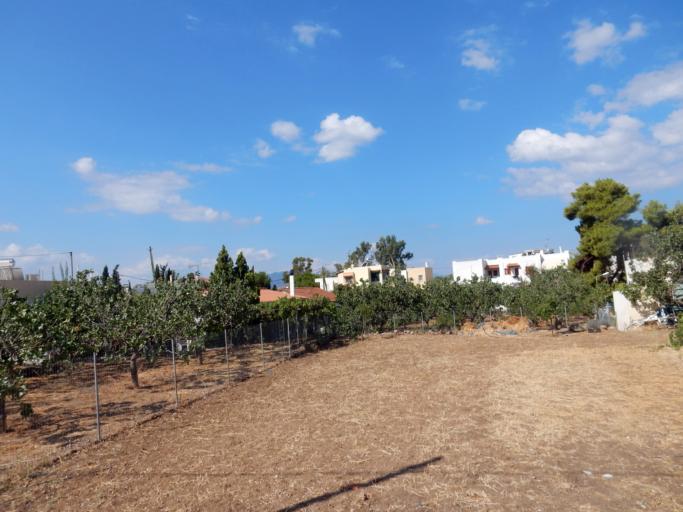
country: GR
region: Attica
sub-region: Nomos Piraios
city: Kypseli
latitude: 37.7186
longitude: 23.4615
